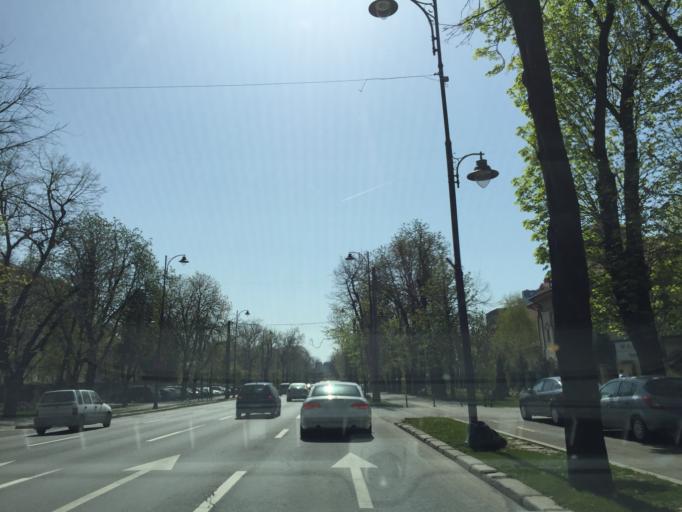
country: RO
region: Bucuresti
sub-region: Municipiul Bucuresti
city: Bucuresti
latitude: 44.4608
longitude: 26.0812
